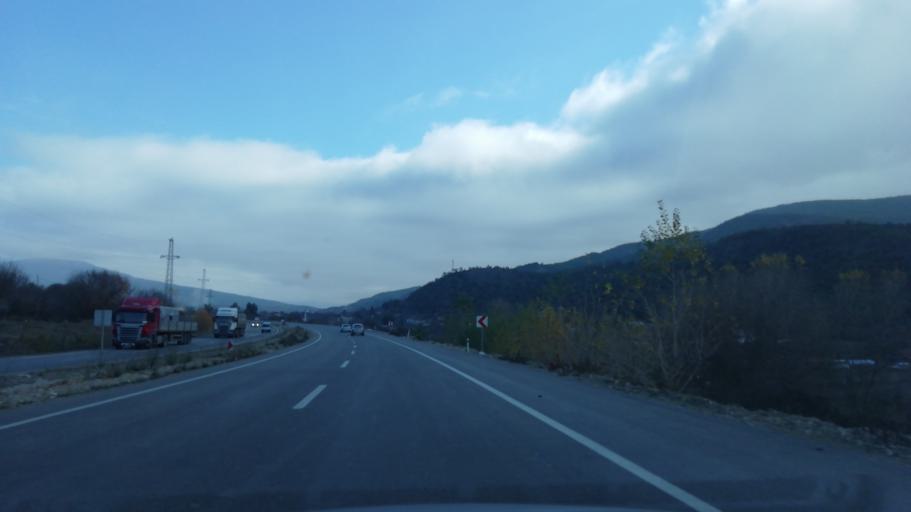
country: TR
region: Karabuk
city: Safranbolu
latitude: 41.2170
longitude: 32.7319
